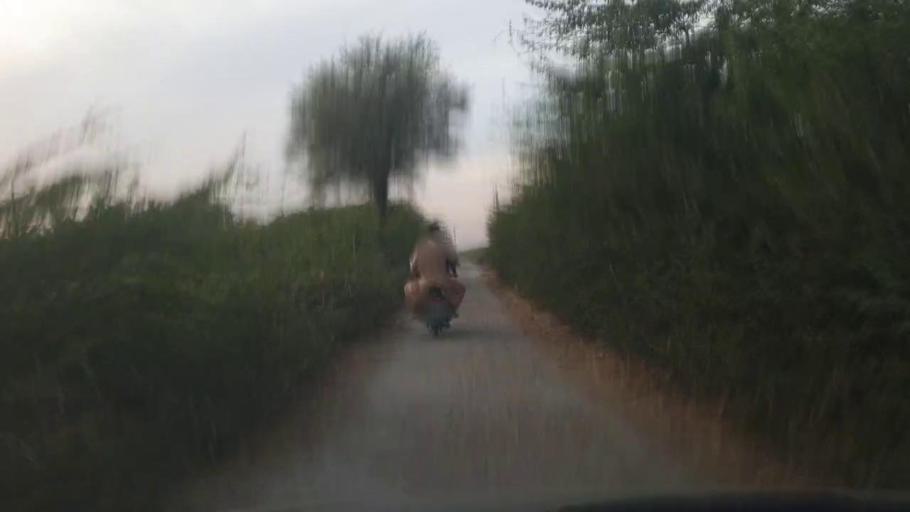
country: PK
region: Sindh
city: Kunri
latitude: 25.2271
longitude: 69.5357
